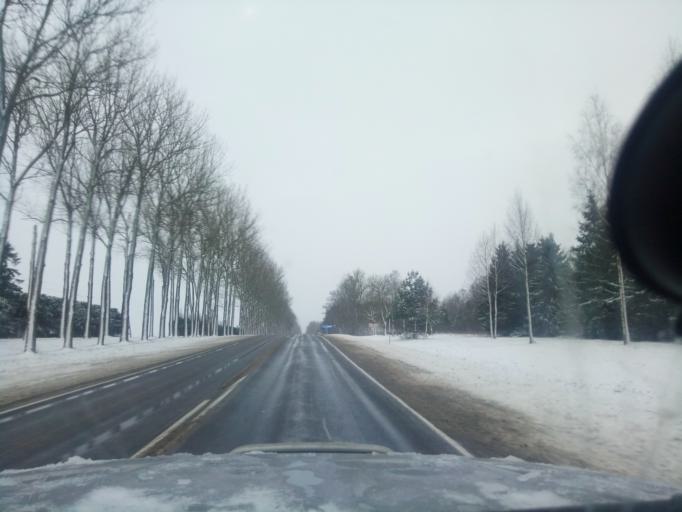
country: BY
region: Minsk
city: Haradzyeya
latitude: 53.3409
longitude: 26.5202
